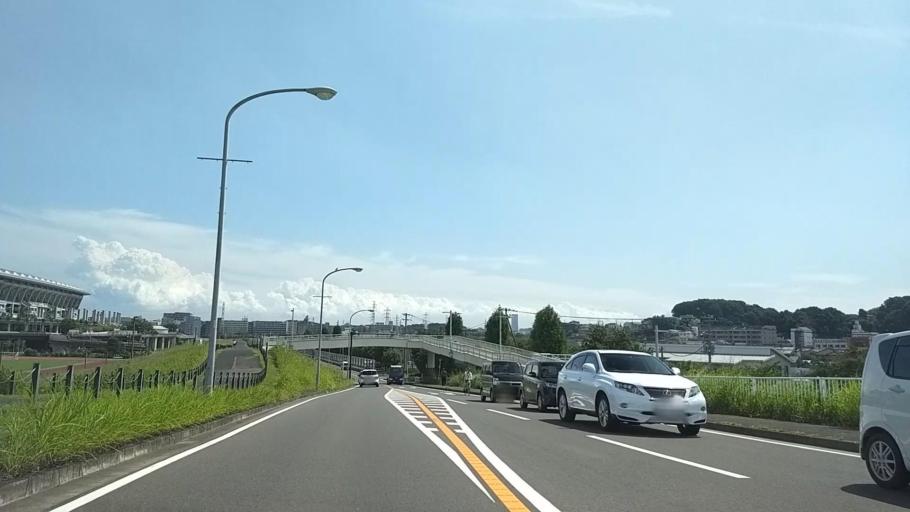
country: JP
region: Kanagawa
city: Yokohama
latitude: 35.5118
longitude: 139.6004
